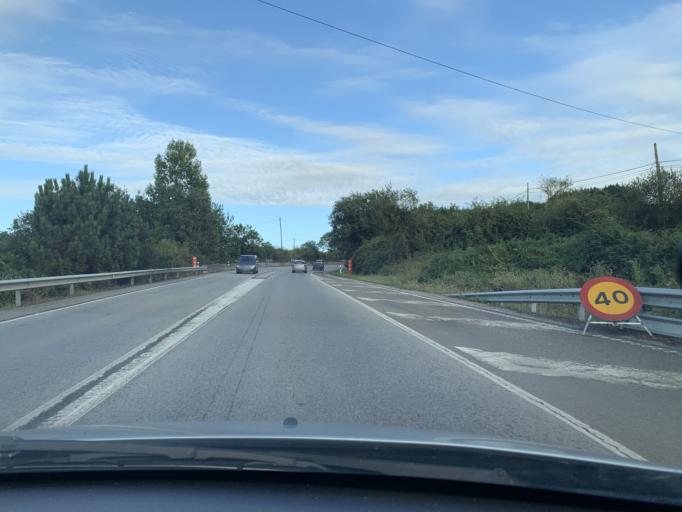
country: ES
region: Galicia
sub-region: Provincia de Lugo
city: Foz
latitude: 43.5549
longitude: -7.2683
